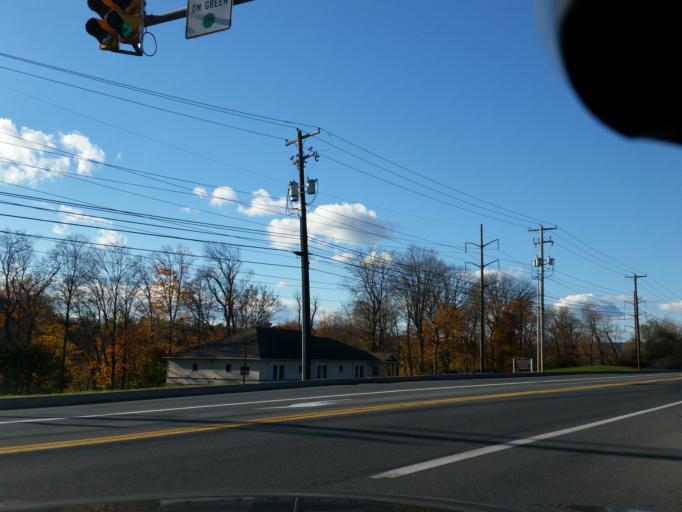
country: US
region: Pennsylvania
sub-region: Cumberland County
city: Wormleysburg
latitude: 40.2597
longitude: -76.9316
